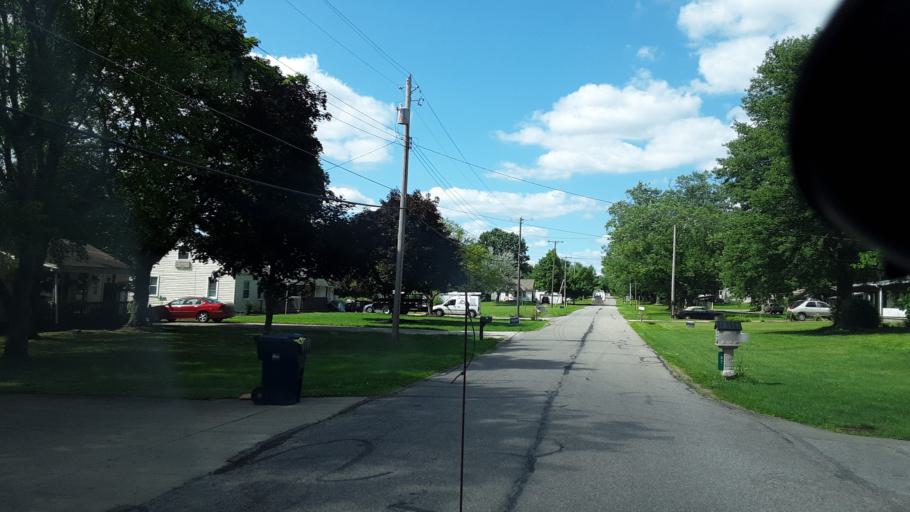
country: US
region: Ohio
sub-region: Richland County
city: Lincoln Heights
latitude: 40.7550
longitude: -82.4729
